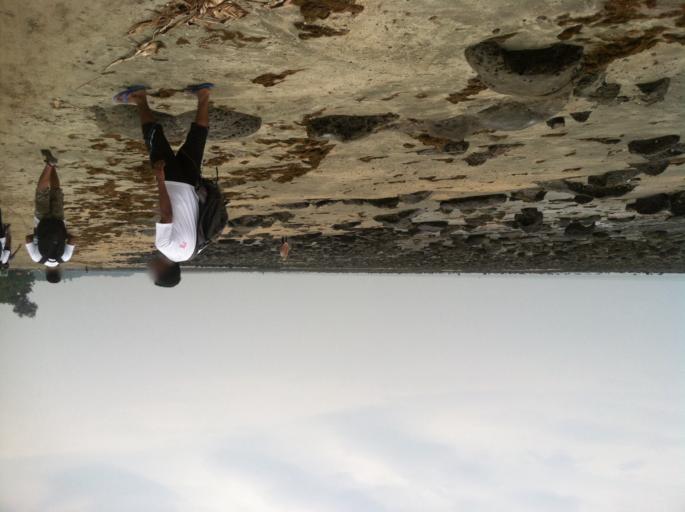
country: BD
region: Chittagong
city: Teknaf
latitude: 20.6258
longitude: 92.3265
